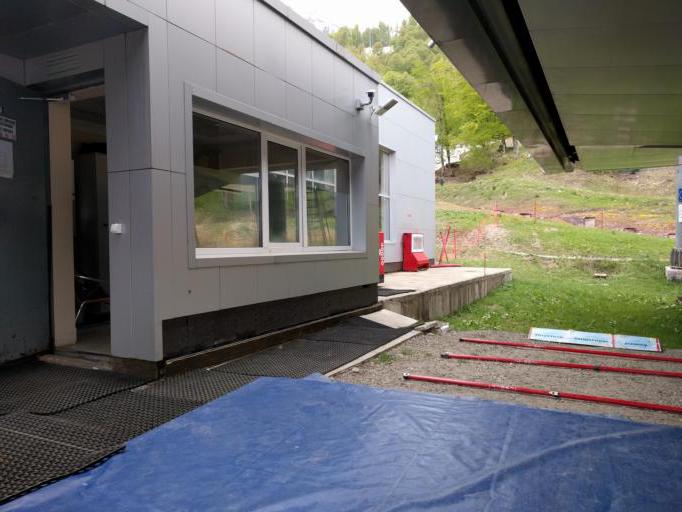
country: RU
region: Krasnodarskiy
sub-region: Sochi City
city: Krasnaya Polyana
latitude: 43.6475
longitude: 40.3317
